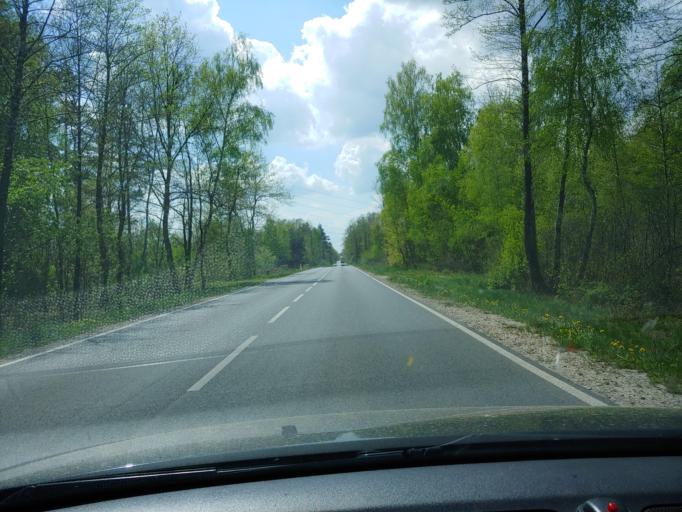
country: PL
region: Lesser Poland Voivodeship
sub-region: Powiat tarnowski
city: Jodlowka-Walki
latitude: 50.1059
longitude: 21.1026
